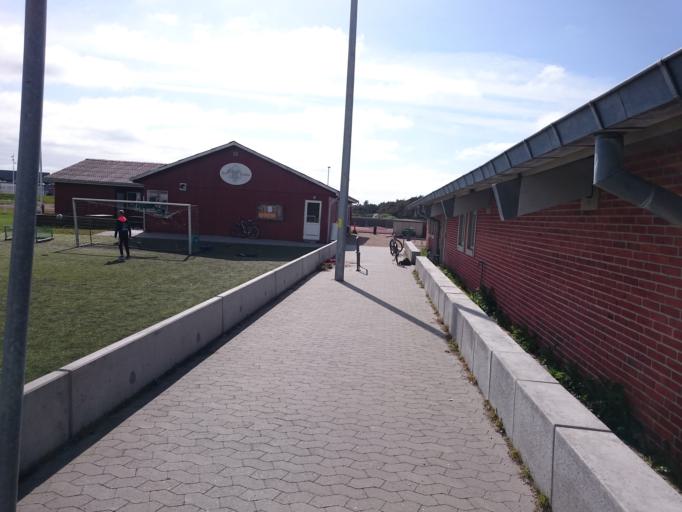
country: DK
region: South Denmark
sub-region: Fano Kommune
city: Nordby
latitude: 55.4469
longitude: 8.3961
